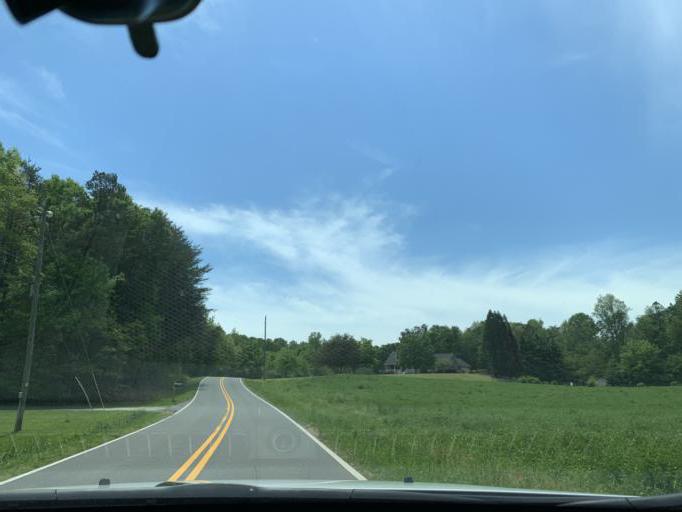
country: US
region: Georgia
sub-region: Hall County
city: Flowery Branch
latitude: 34.2896
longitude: -84.0167
